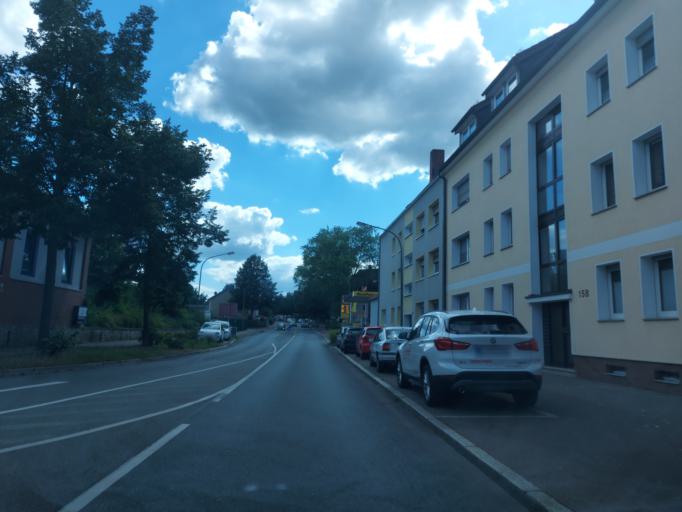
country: DE
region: Lower Saxony
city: Osnabrueck
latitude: 52.2567
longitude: 8.0427
